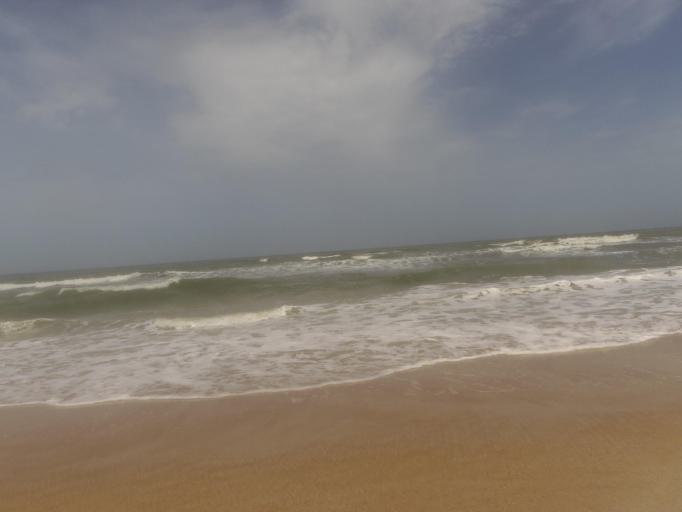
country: US
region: Florida
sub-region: Saint Johns County
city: Saint Augustine
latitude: 29.8902
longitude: -81.2746
